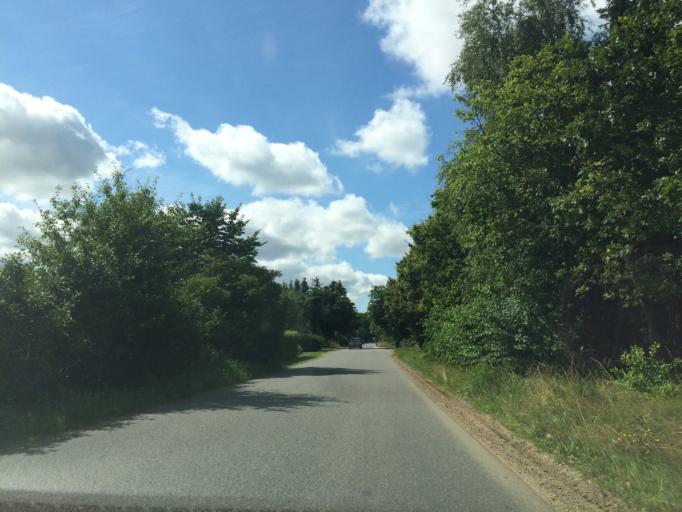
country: DK
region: Central Jutland
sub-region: Silkeborg Kommune
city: Svejbaek
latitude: 56.2130
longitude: 9.6823
